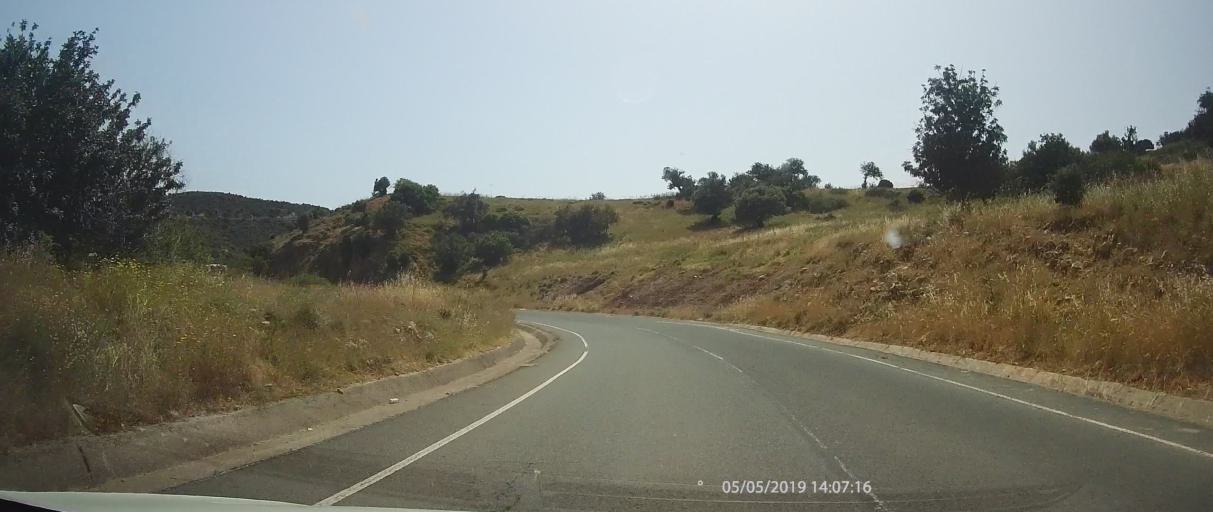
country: CY
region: Limassol
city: Pissouri
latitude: 34.7362
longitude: 32.5996
